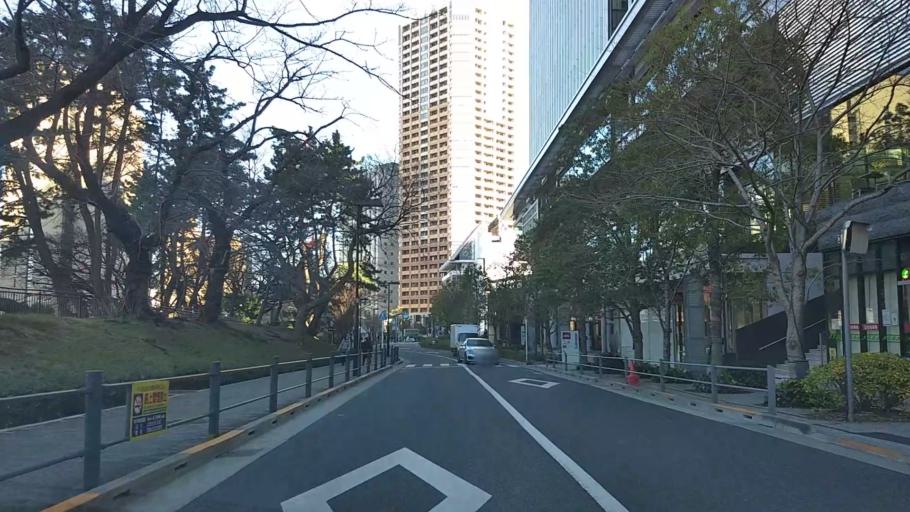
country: JP
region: Tokyo
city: Tokyo
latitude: 35.6985
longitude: 139.7428
